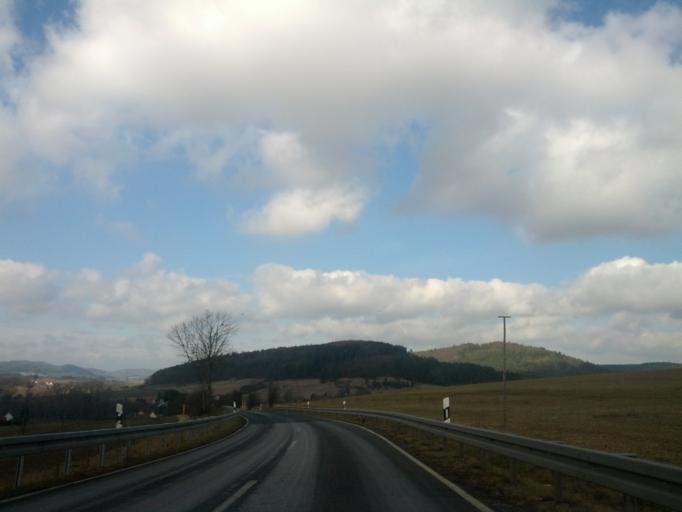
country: DE
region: Thuringia
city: Krauthausen
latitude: 51.0125
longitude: 10.2945
